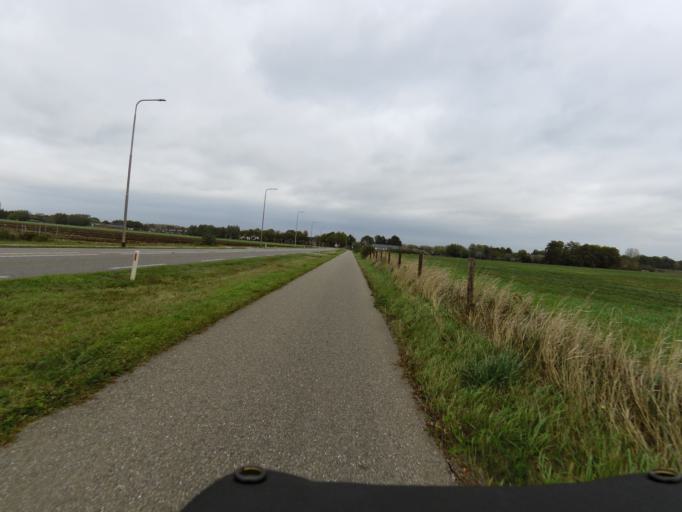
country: NL
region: Gelderland
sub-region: Gemeente Zevenaar
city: Zevenaar
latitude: 51.9012
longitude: 6.1094
